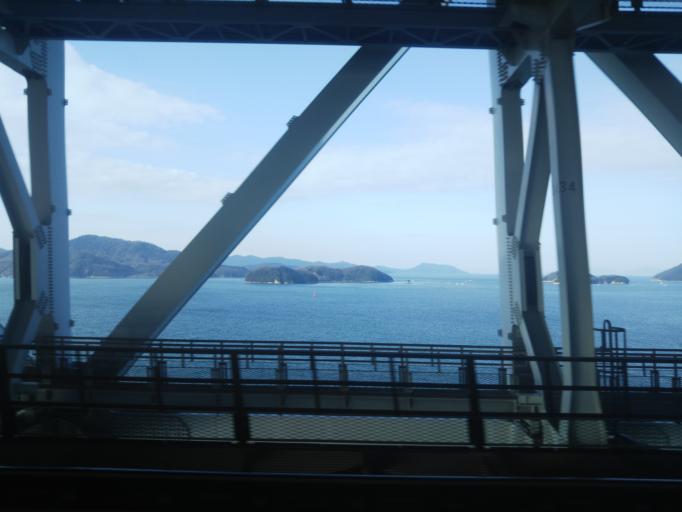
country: JP
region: Kagawa
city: Sakaidecho
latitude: 34.4097
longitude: 133.8070
